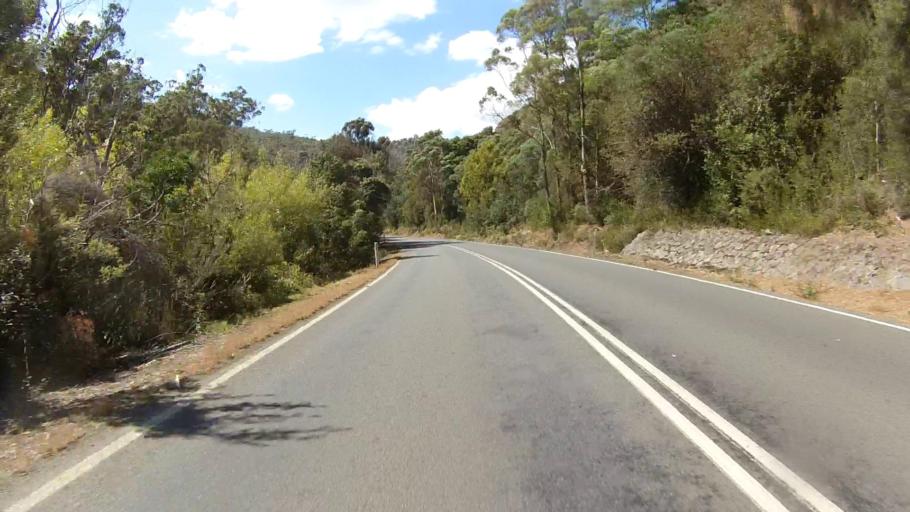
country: AU
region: Tasmania
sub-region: Derwent Valley
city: New Norfolk
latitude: -42.6770
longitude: 146.7596
